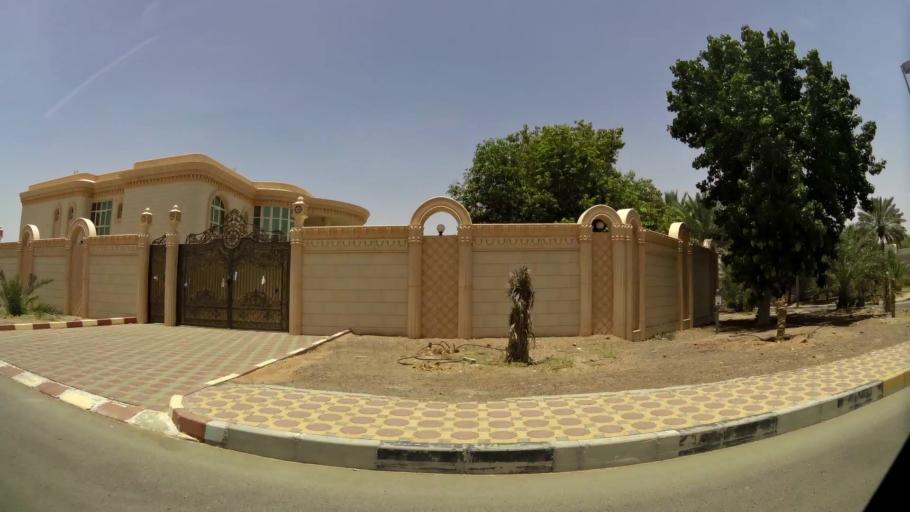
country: OM
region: Al Buraimi
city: Al Buraymi
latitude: 24.2658
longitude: 55.7273
